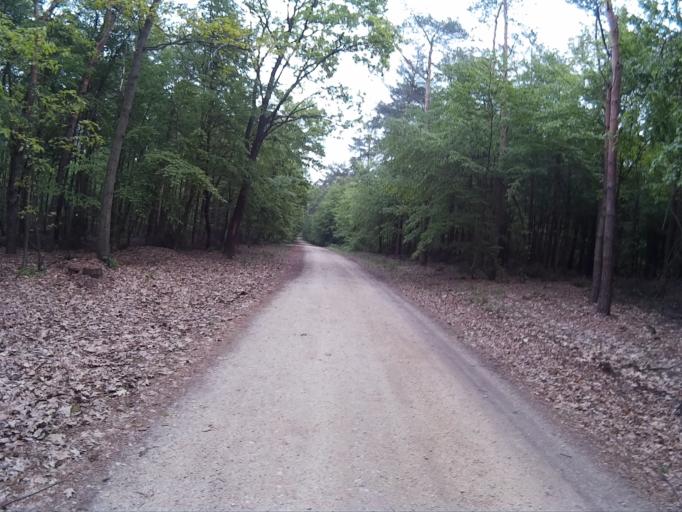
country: HU
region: Vas
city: Vasvar
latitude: 47.0677
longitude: 16.8908
